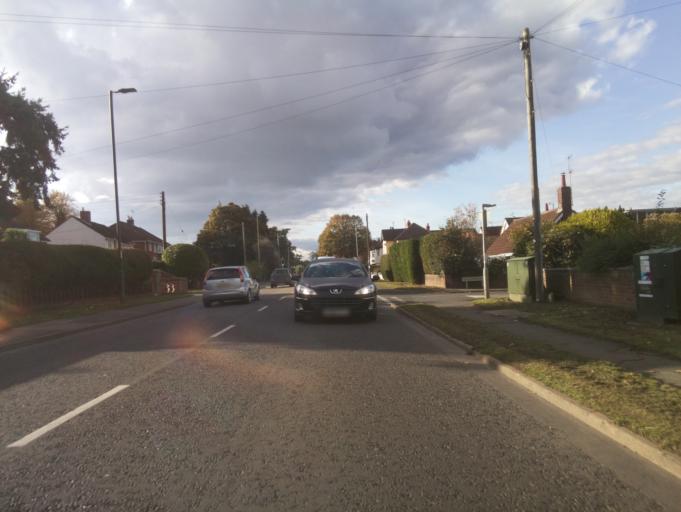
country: GB
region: England
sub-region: Herefordshire
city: Belmont
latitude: 52.0635
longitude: -2.7449
